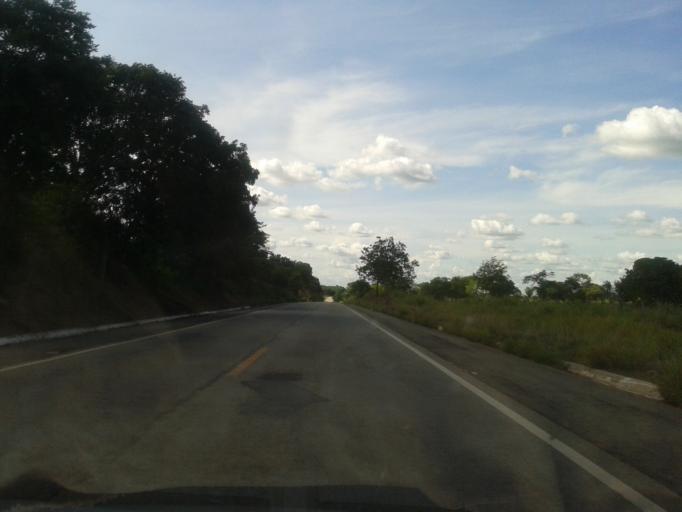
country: BR
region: Goias
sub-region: Mozarlandia
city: Mozarlandia
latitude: -15.2245
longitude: -50.5251
